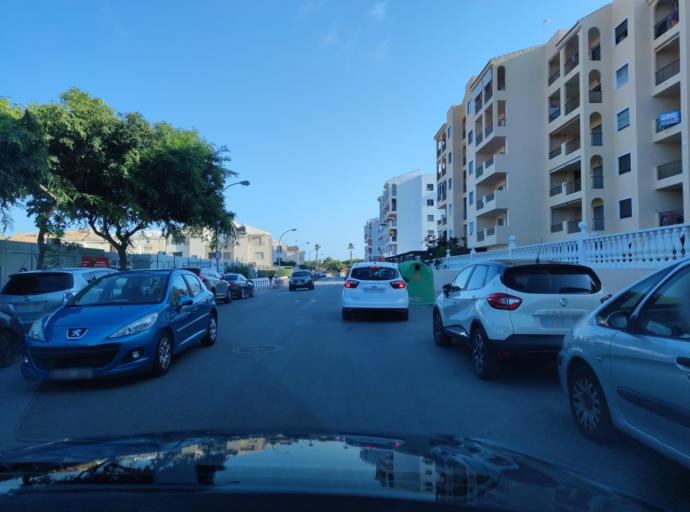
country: ES
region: Valencia
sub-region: Provincia de Alicante
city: Guardamar del Segura
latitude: 38.0818
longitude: -0.6516
